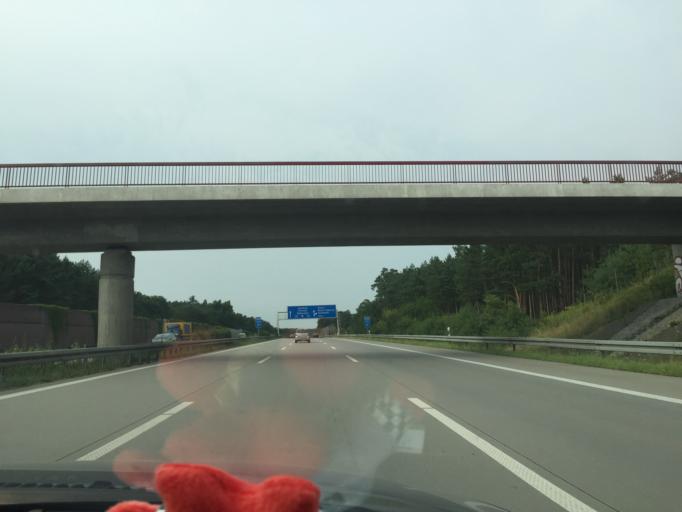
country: DE
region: Brandenburg
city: Grunheide
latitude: 52.4121
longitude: 13.7860
